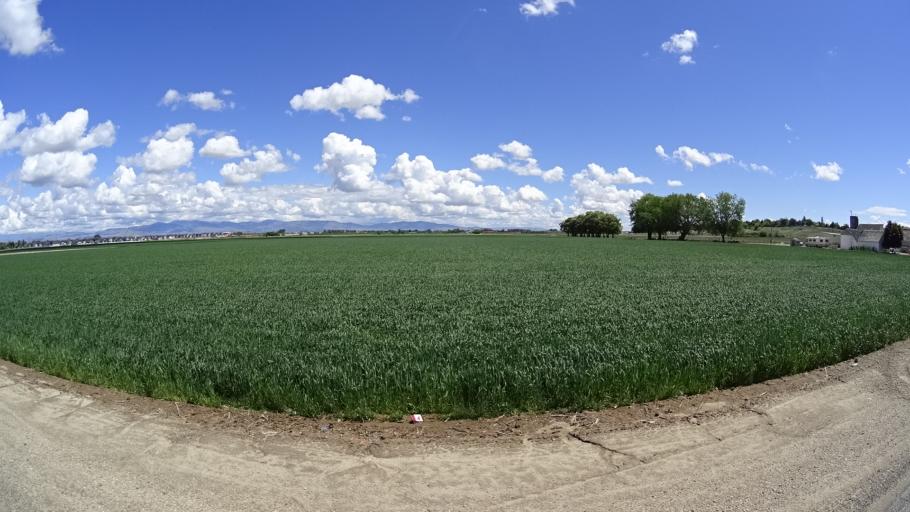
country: US
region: Idaho
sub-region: Ada County
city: Meridian
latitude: 43.5983
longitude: -116.4536
